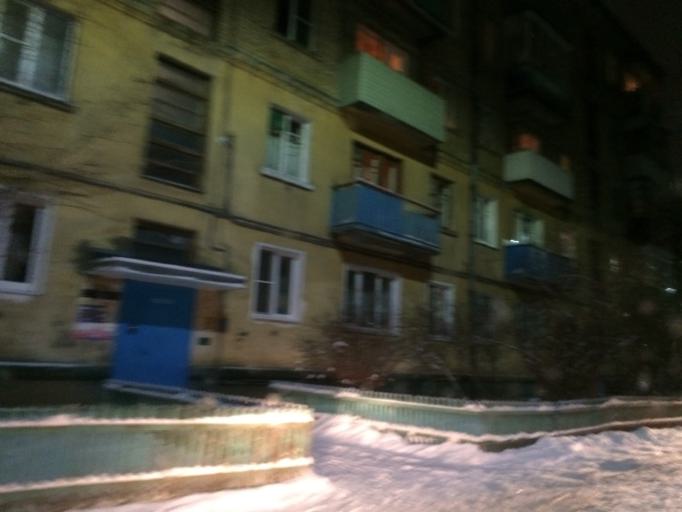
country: RU
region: Tula
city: Mendeleyevskiy
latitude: 54.1642
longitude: 37.5891
